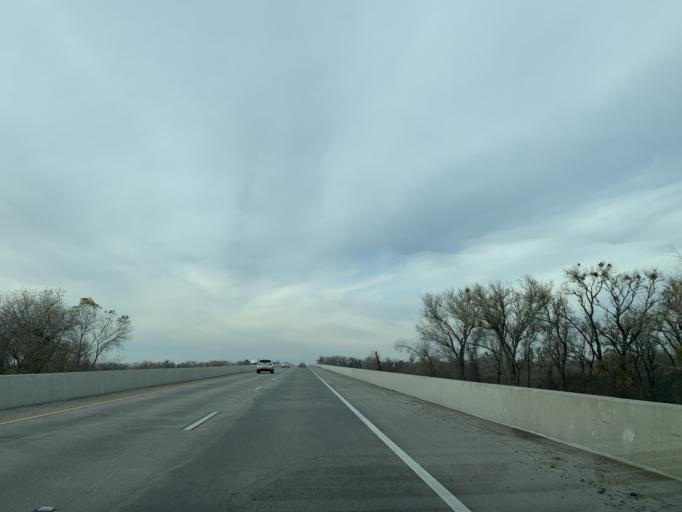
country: US
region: California
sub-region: Yuba County
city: Plumas Lake
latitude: 38.8996
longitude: -121.5847
